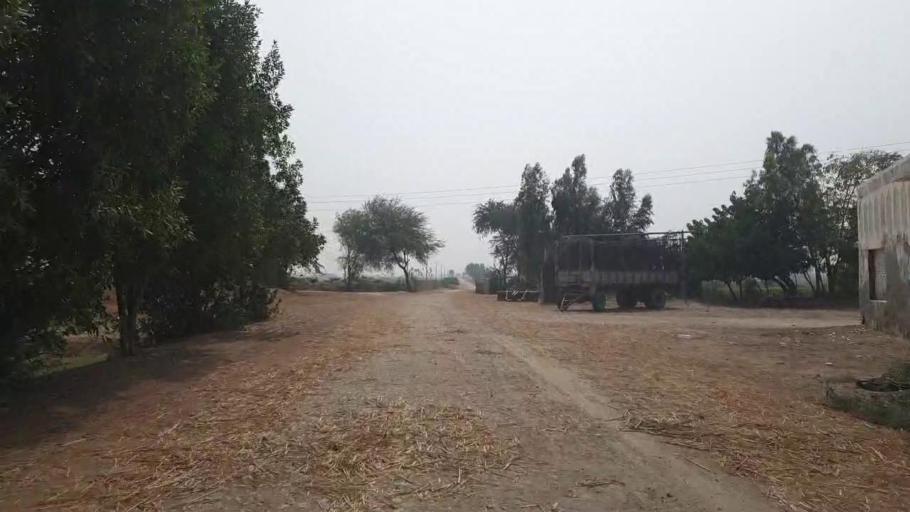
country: PK
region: Sindh
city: Kario
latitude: 24.6443
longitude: 68.6218
